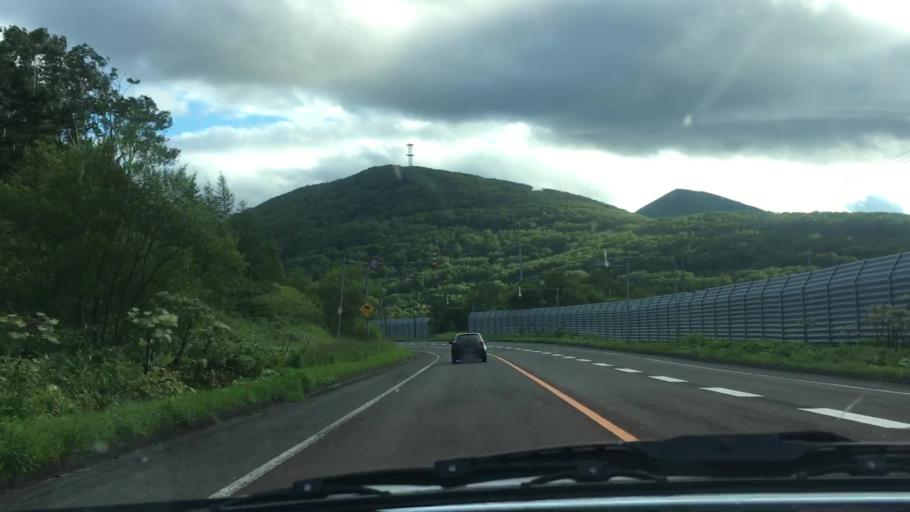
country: JP
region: Hokkaido
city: Shimo-furano
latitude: 43.1343
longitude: 142.7632
